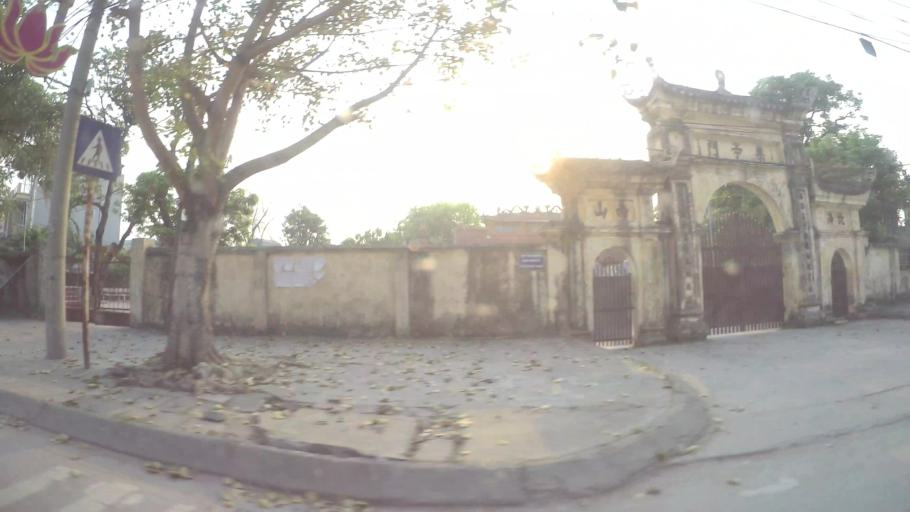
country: VN
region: Ha Noi
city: Van Dien
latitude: 20.9281
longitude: 105.8358
